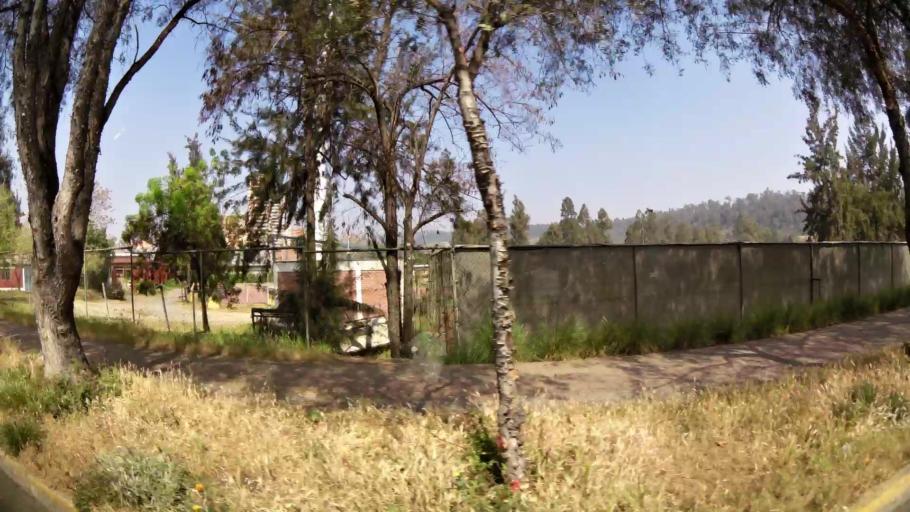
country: CL
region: Santiago Metropolitan
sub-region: Provincia de Santiago
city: Villa Presidente Frei, Nunoa, Santiago, Chile
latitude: -33.3921
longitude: -70.5975
